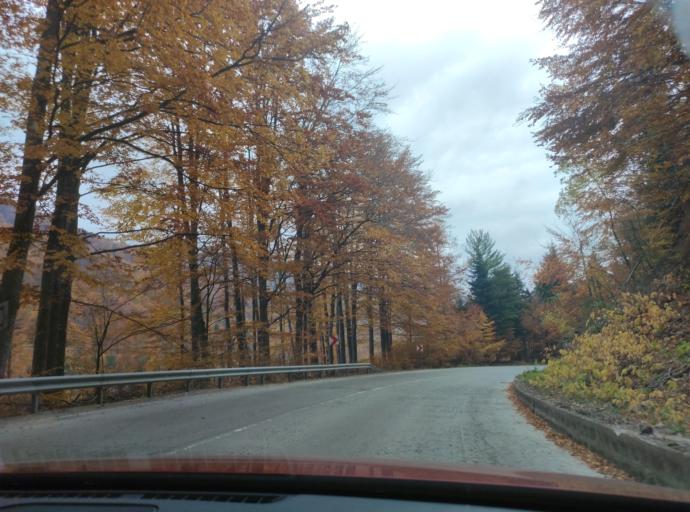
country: BG
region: Montana
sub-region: Obshtina Berkovitsa
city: Berkovitsa
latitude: 43.1378
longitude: 23.1419
